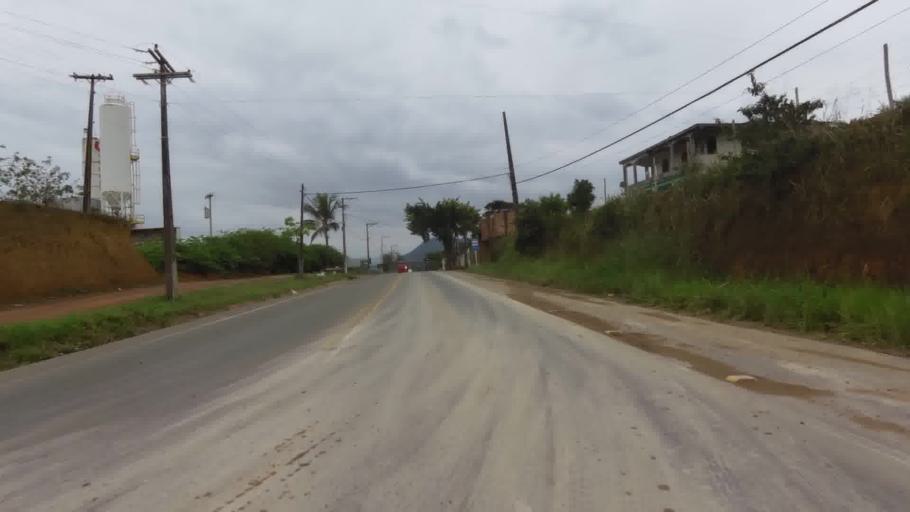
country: BR
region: Espirito Santo
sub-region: Piuma
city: Piuma
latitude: -20.8199
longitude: -40.7331
